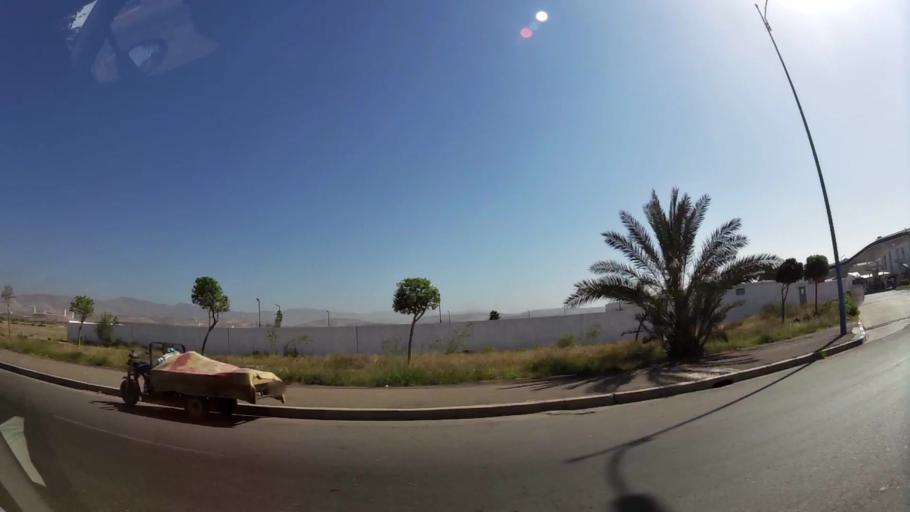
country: MA
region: Oued ed Dahab-Lagouira
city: Dakhla
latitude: 30.4065
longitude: -9.5355
